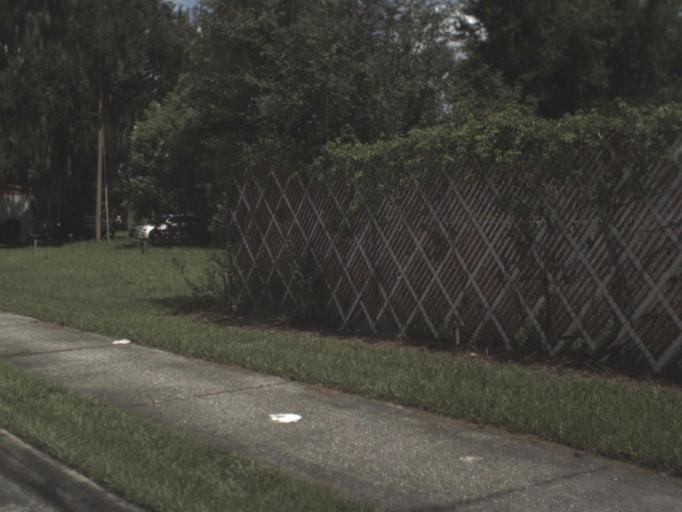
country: US
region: Florida
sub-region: Polk County
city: Bartow
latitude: 27.8946
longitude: -81.8286
